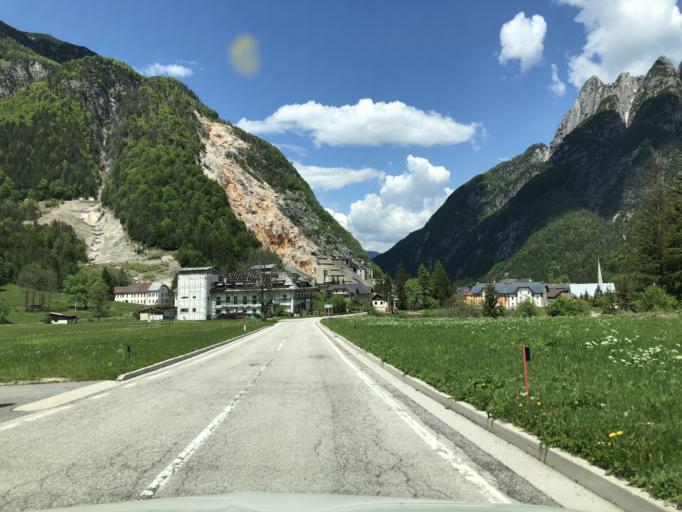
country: IT
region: Friuli Venezia Giulia
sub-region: Provincia di Udine
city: Tarvisio
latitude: 46.4361
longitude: 13.5680
